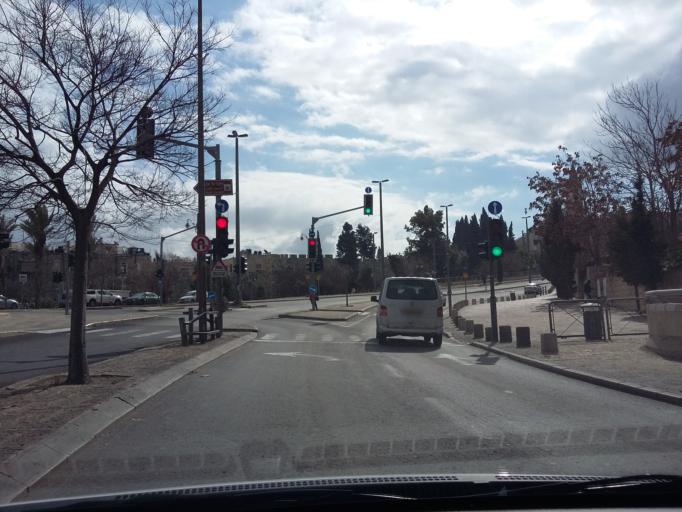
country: PS
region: West Bank
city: East Jerusalem
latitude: 31.7817
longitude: 35.2280
